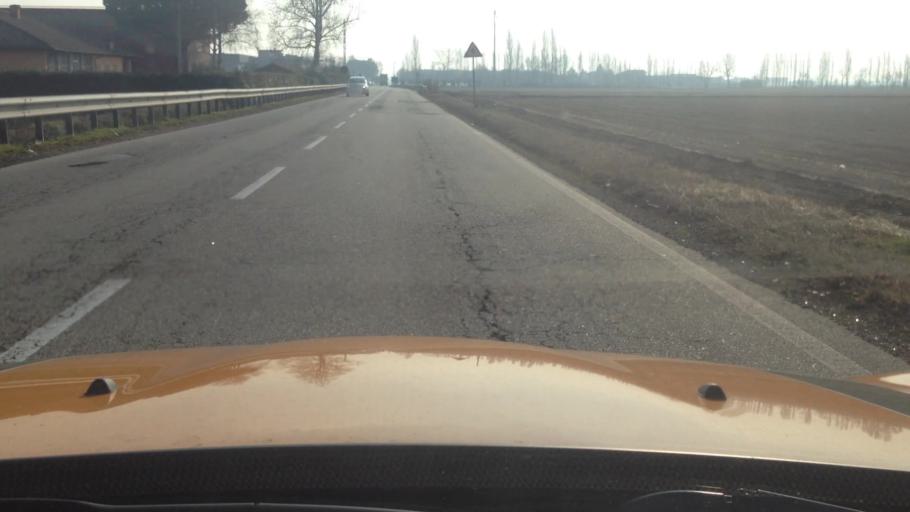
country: IT
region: Piedmont
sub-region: Provincia di Novara
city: San Pietro Mosezzo
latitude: 45.4644
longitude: 8.5582
